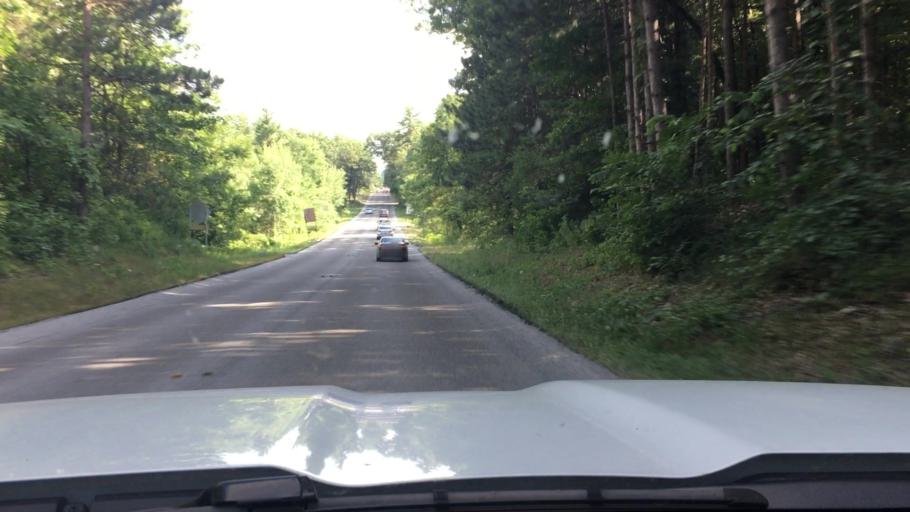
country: US
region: Michigan
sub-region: Montcalm County
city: Greenville
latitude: 43.1722
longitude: -85.3528
